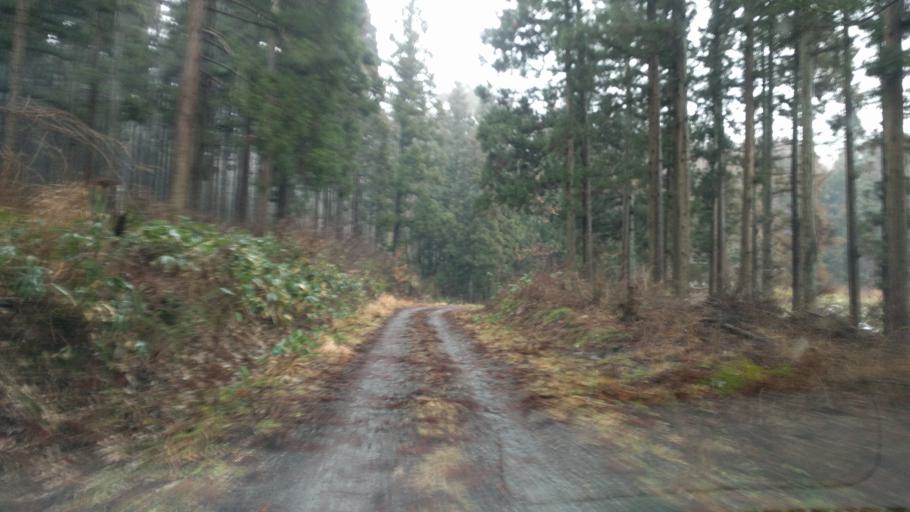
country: JP
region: Fukushima
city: Kitakata
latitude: 37.5777
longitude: 139.9778
